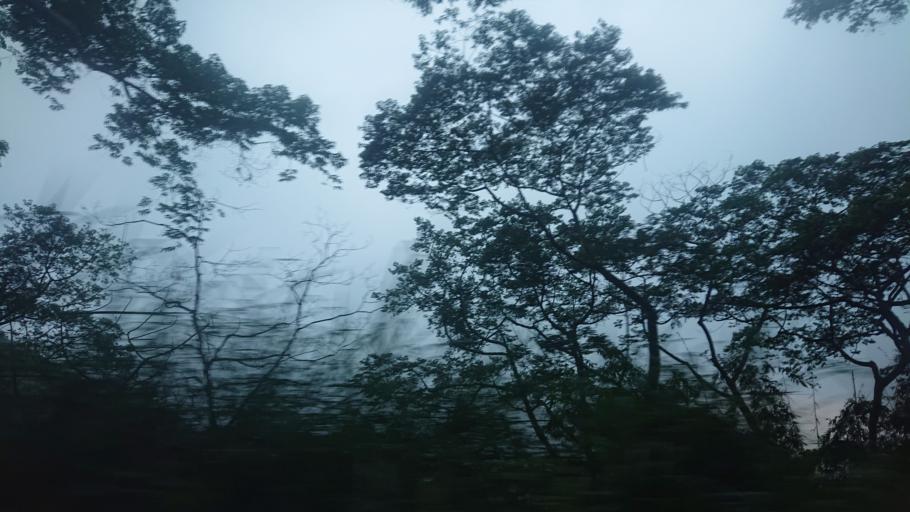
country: TW
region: Taiwan
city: Lugu
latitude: 23.5887
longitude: 120.7260
